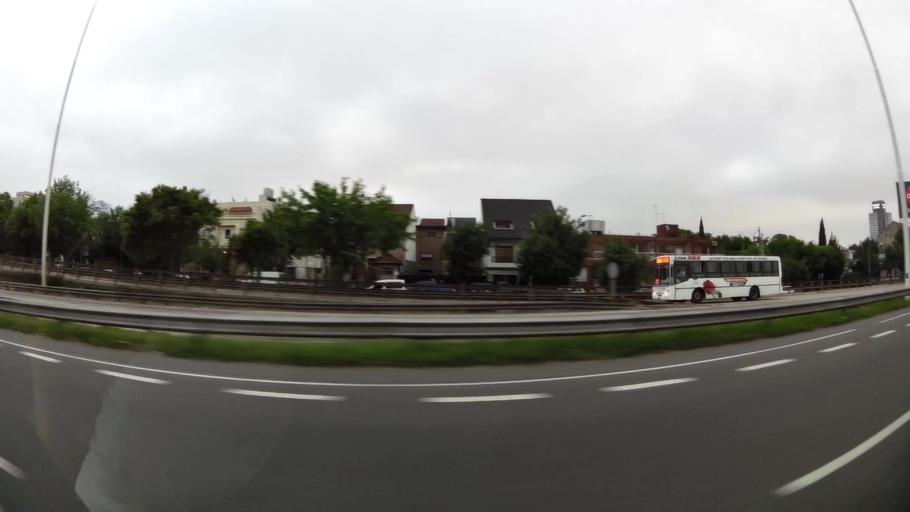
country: AR
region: Buenos Aires
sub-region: Partido de Vicente Lopez
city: Olivos
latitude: -34.5421
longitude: -58.4824
